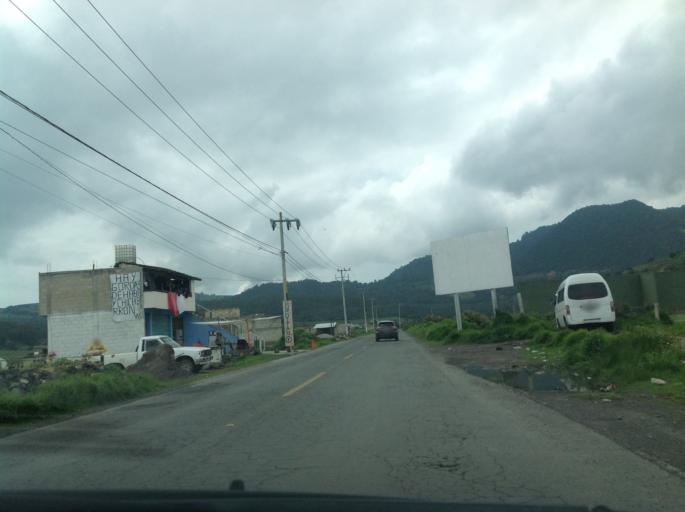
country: MX
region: Mexico
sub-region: Tenango del Valle
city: Santa Maria Jajalpa
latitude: 19.1120
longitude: -99.5303
